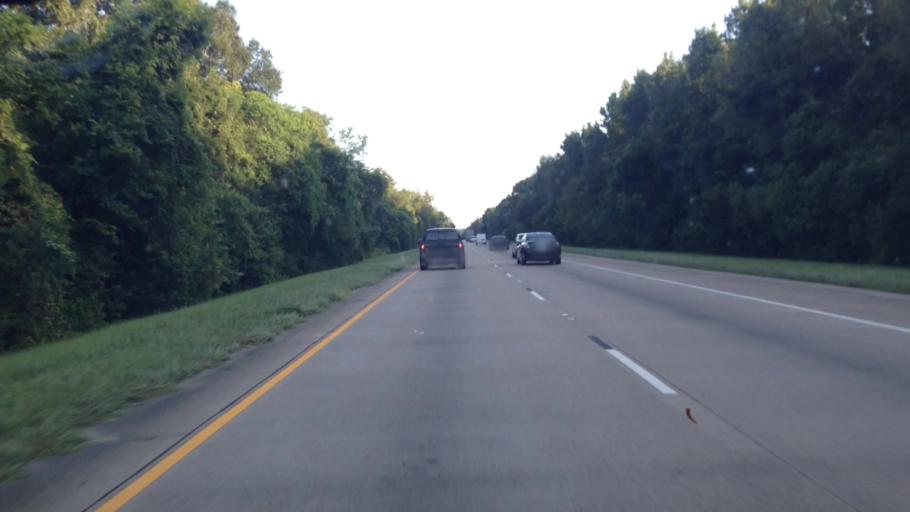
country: US
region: Louisiana
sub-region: Ascension Parish
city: Prairieville
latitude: 30.2884
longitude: -90.9900
